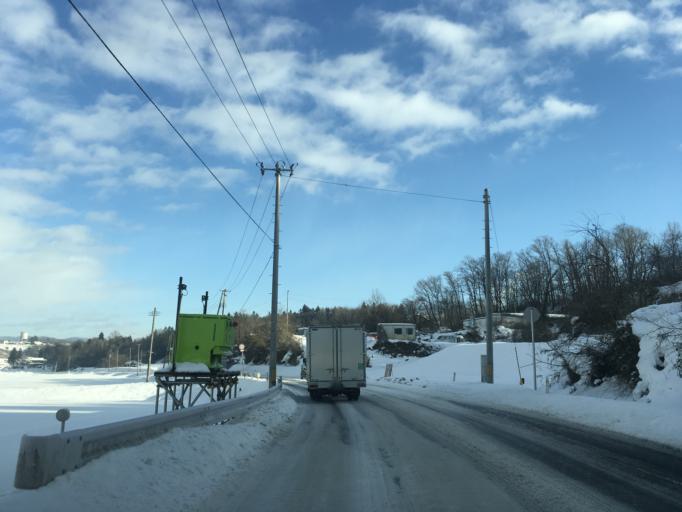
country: JP
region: Iwate
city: Ichinoseki
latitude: 38.8926
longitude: 141.1580
